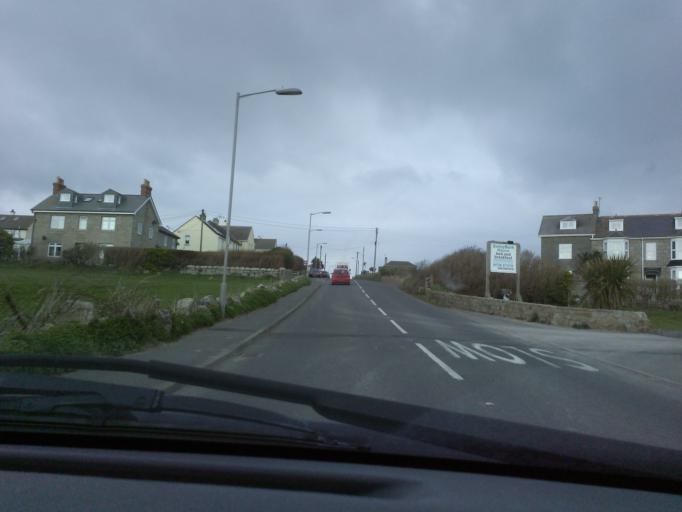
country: GB
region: England
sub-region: Cornwall
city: Sennen
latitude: 50.0780
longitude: -5.6843
